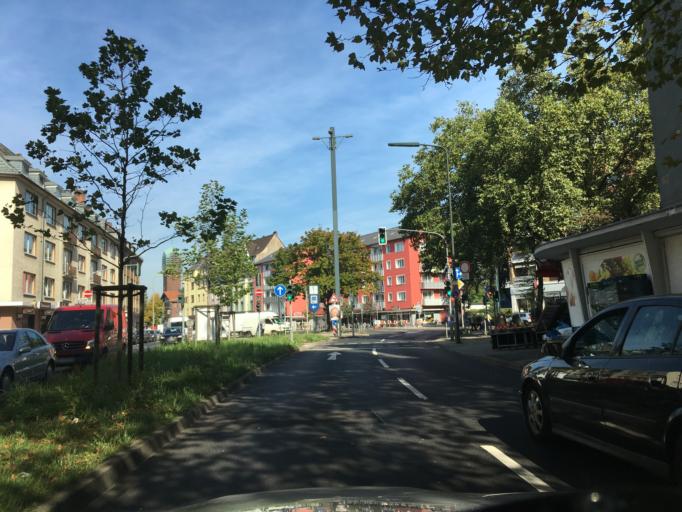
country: DE
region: North Rhine-Westphalia
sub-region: Regierungsbezirk Dusseldorf
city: Dusseldorf
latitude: 51.2064
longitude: 6.8316
